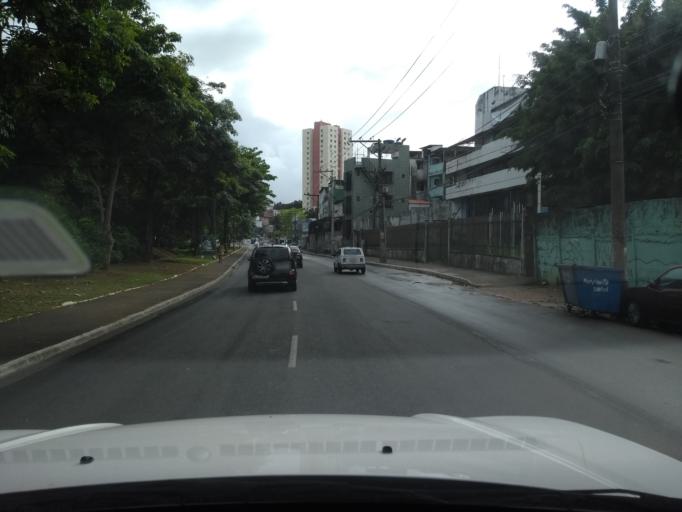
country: BR
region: Bahia
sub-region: Salvador
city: Salvador
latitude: -12.9926
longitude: -38.5125
